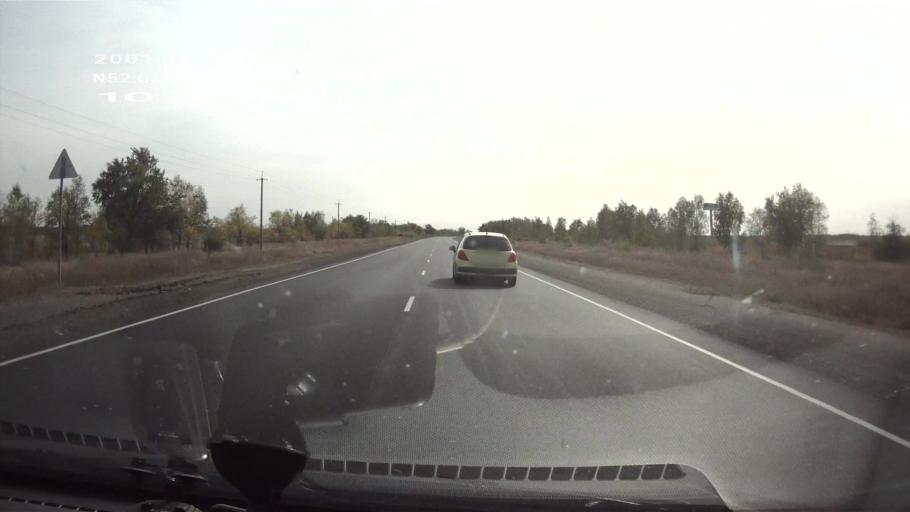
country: RU
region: Saratov
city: Sinodskoye
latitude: 52.0380
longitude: 46.7301
